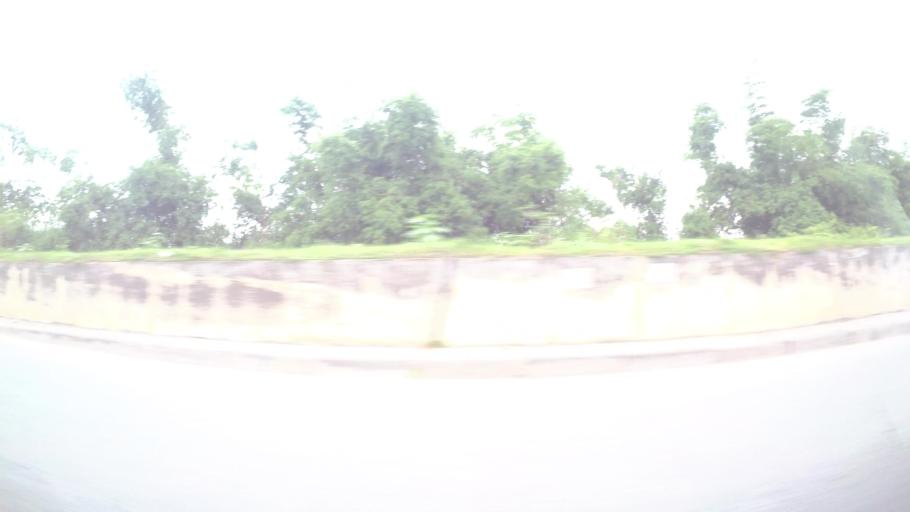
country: VN
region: Ha Noi
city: Trau Quy
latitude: 21.0550
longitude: 105.9218
